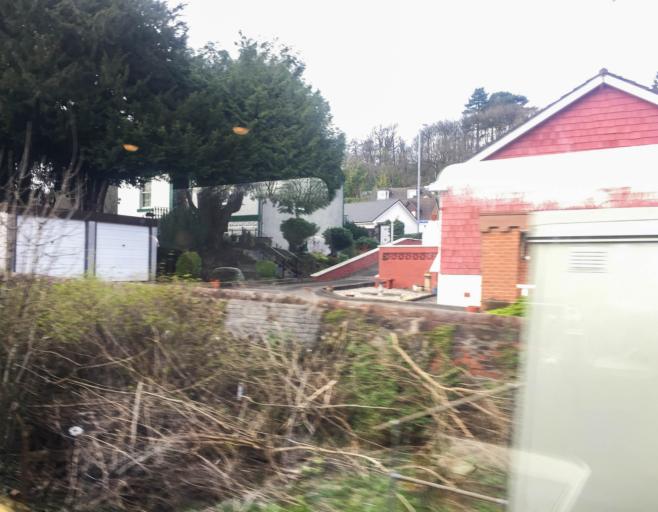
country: GB
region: Scotland
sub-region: Renfrewshire
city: Bishopton
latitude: 55.9311
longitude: -4.4950
